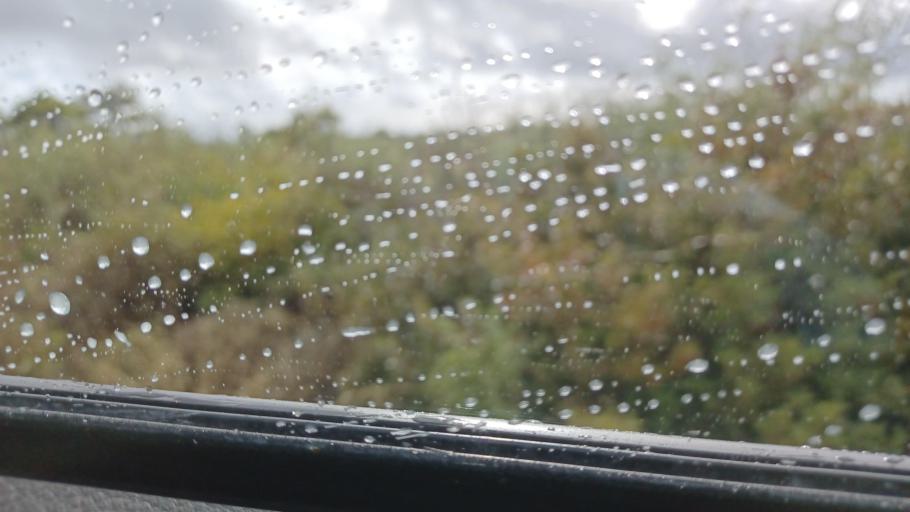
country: CY
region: Limassol
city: Sotira
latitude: 34.7444
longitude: 32.8529
